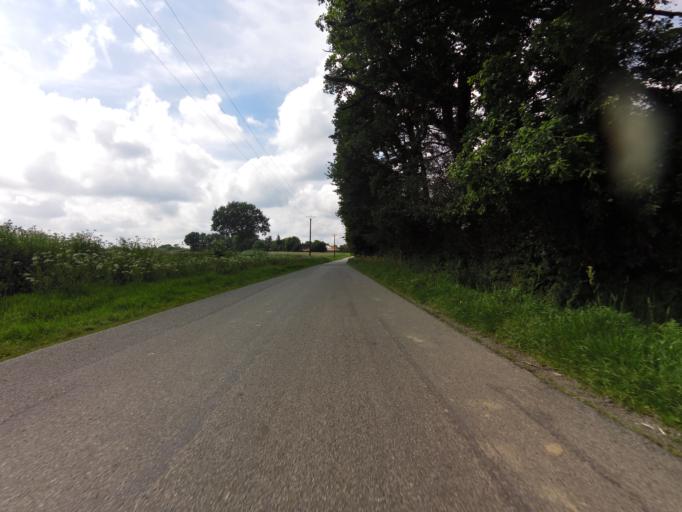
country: FR
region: Brittany
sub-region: Departement du Morbihan
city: Malansac
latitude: 47.6851
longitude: -2.3093
